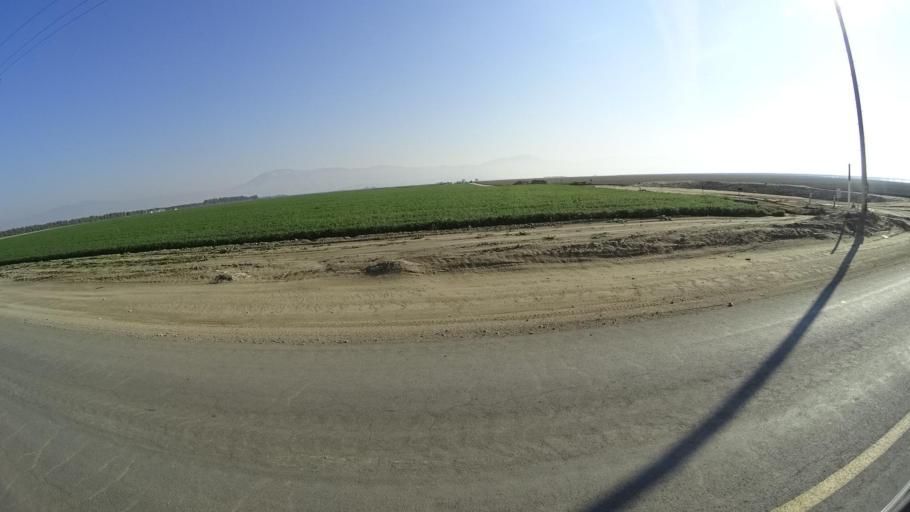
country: US
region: California
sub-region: Kern County
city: Weedpatch
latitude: 35.1010
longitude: -118.9677
